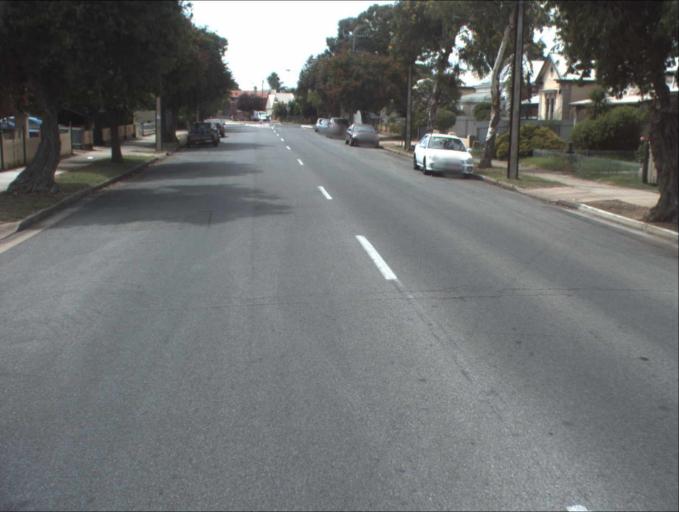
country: AU
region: South Australia
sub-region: Port Adelaide Enfield
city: Alberton
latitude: -34.8593
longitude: 138.5169
